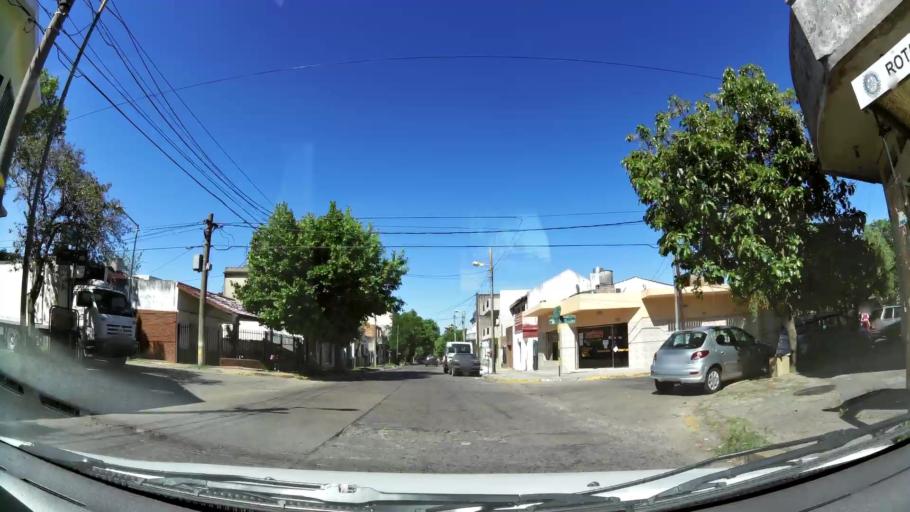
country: AR
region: Buenos Aires
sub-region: Partido de General San Martin
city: General San Martin
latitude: -34.5655
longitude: -58.5323
